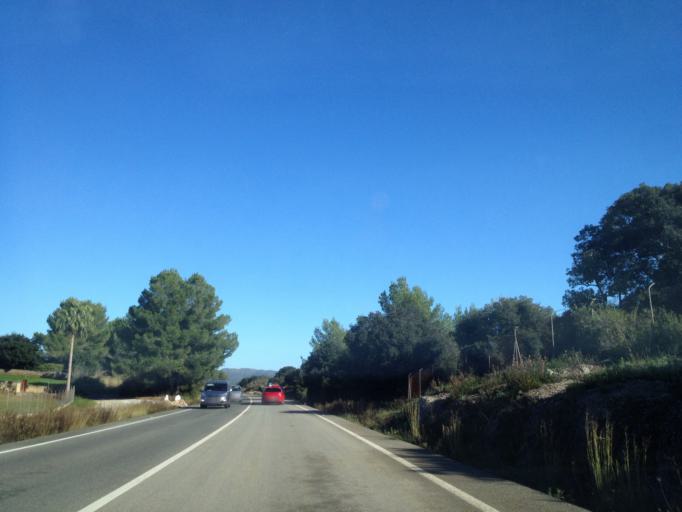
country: ES
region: Balearic Islands
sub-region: Illes Balears
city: Arta
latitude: 39.6661
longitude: 3.3221
